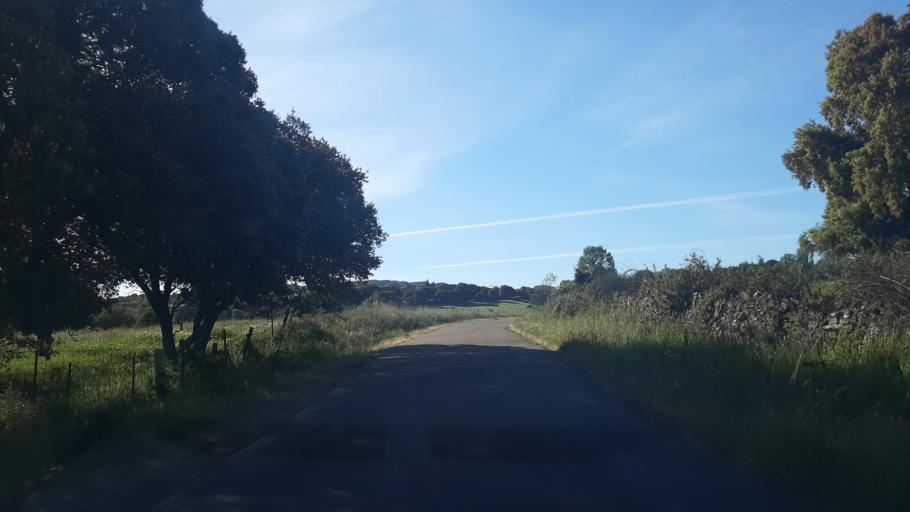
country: ES
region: Castille and Leon
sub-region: Provincia de Salamanca
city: Guijo de Avila
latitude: 40.5342
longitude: -5.6487
